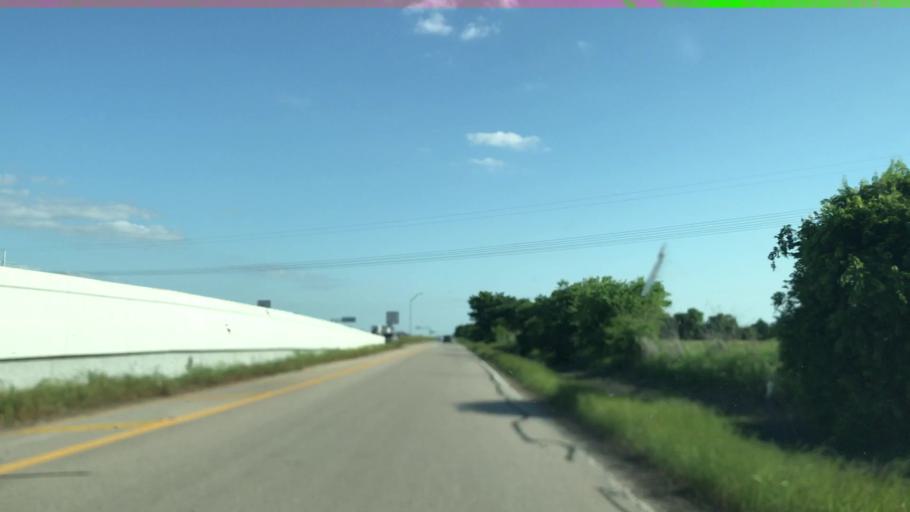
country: US
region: Texas
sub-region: Ellis County
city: Red Oak
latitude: 32.5447
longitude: -96.8226
